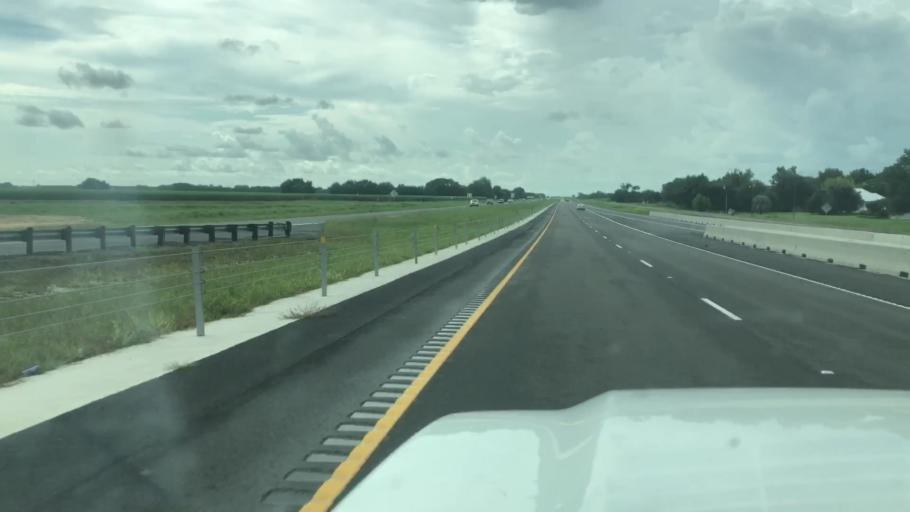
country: US
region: Louisiana
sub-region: Iberia Parish
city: Jeanerette
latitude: 29.8681
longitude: -91.6365
